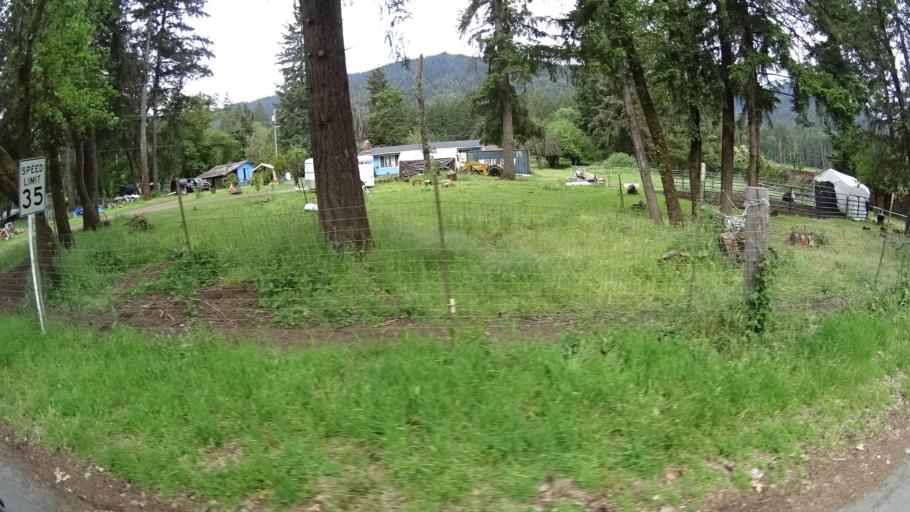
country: US
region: California
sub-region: Humboldt County
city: Willow Creek
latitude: 40.9719
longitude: -123.6305
